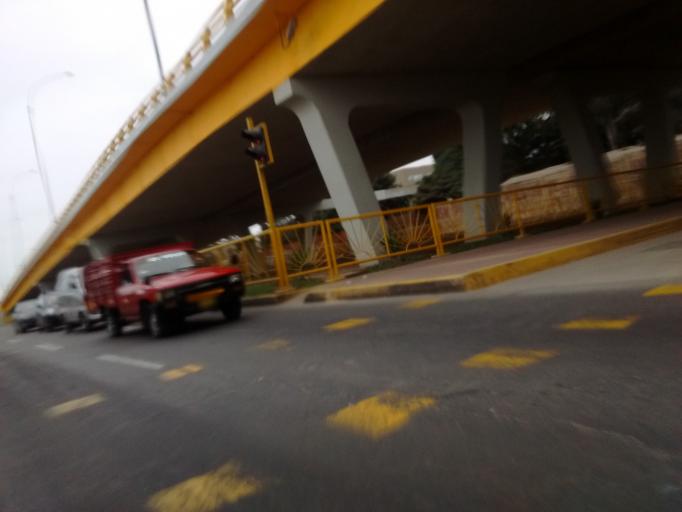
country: PE
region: Callao
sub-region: Callao
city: Callao
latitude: -12.0604
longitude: -77.0793
